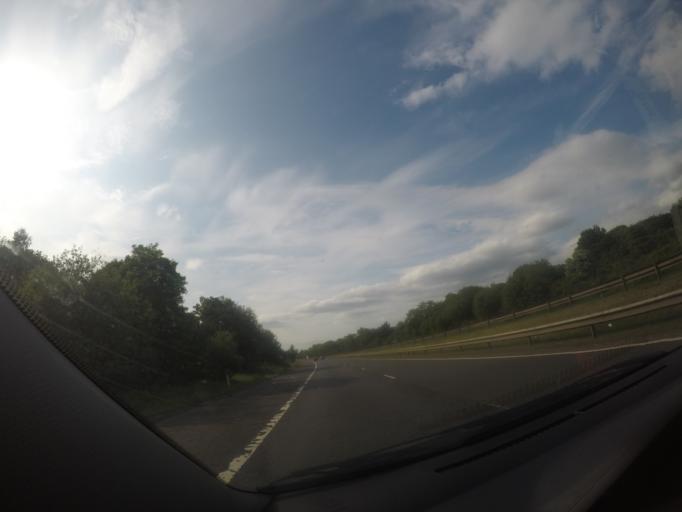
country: GB
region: Scotland
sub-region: South Lanarkshire
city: Larkhall
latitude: 55.7407
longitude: -3.9535
